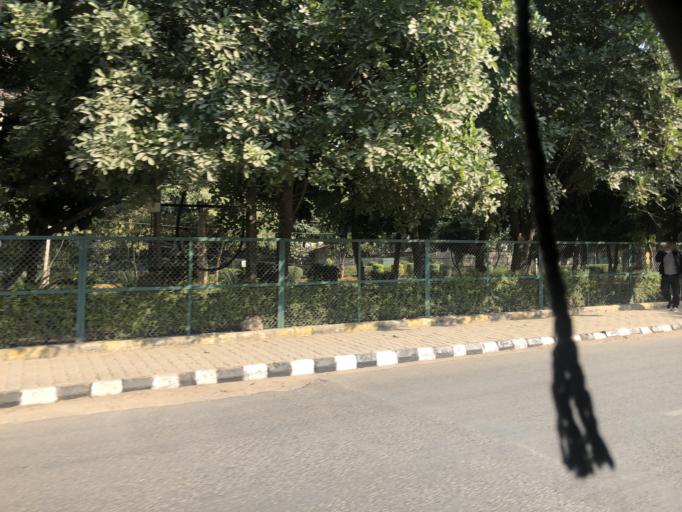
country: IN
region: Haryana
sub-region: Gurgaon
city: Gurgaon
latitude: 28.4570
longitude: 77.0743
